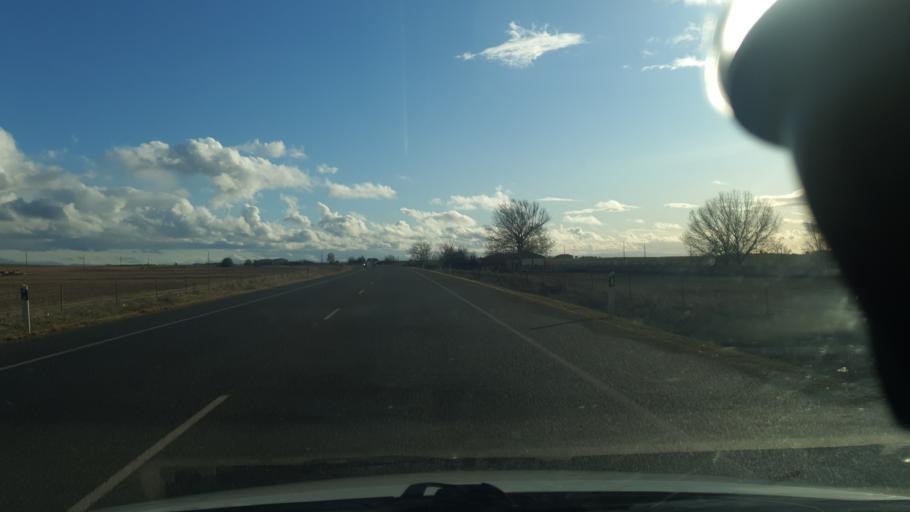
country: ES
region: Castille and Leon
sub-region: Provincia de Segovia
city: San Cristobal de la Vega
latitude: 41.1042
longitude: -4.6388
